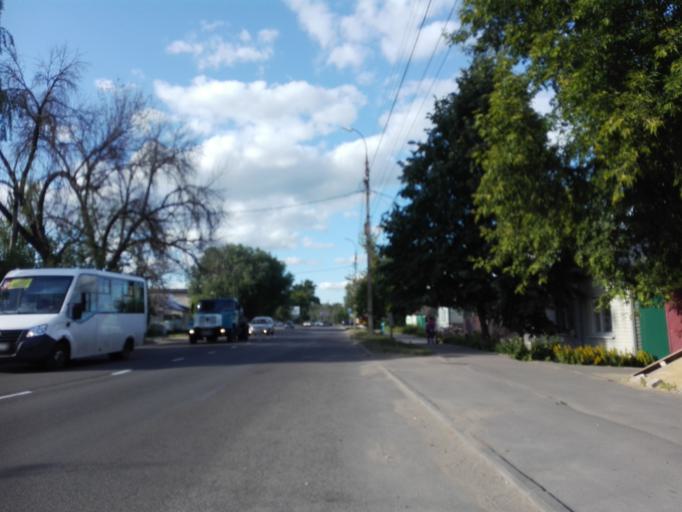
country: RU
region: Orjol
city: Orel
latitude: 52.9444
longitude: 36.0749
